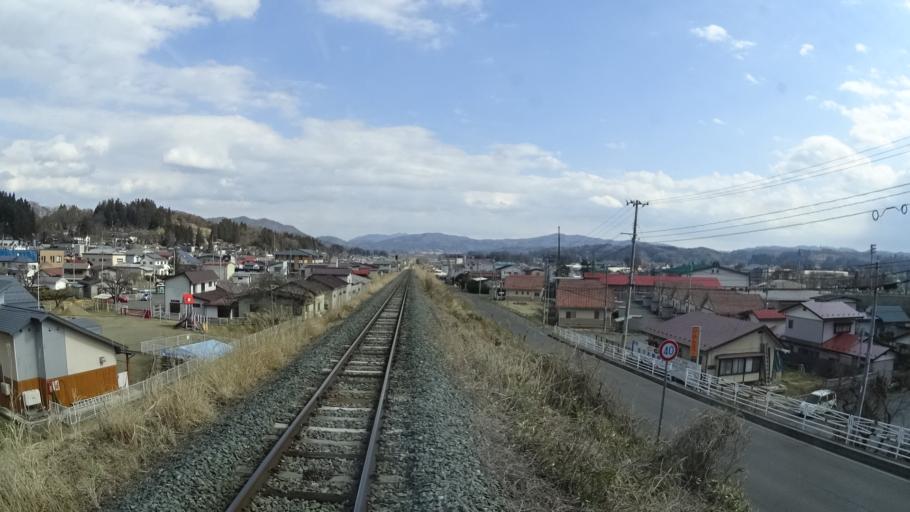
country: JP
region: Iwate
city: Hanamaki
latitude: 39.3880
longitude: 141.2251
